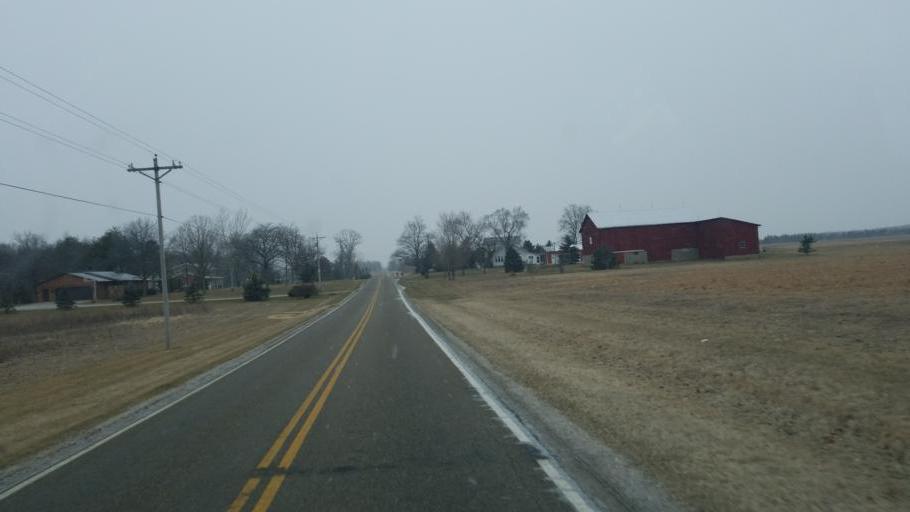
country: US
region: Ohio
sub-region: Defiance County
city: Hicksville
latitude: 41.3249
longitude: -84.7770
